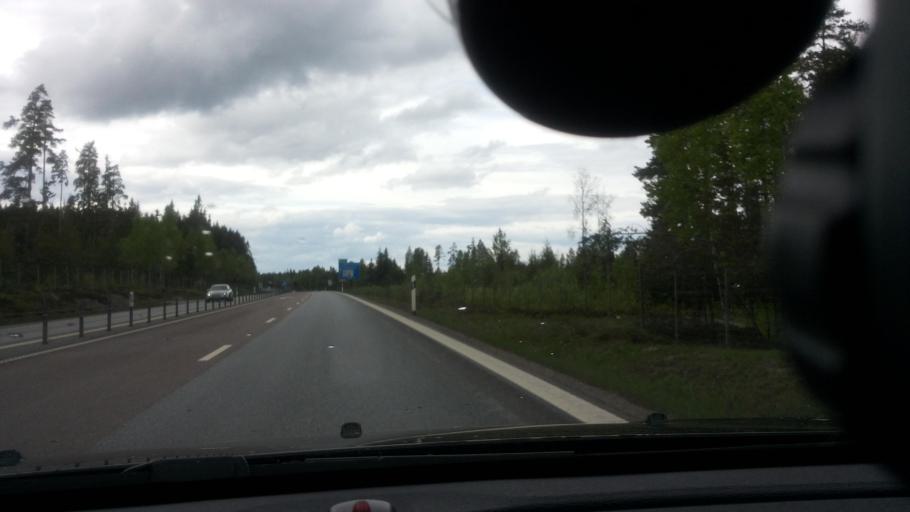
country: SE
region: Gaevleborg
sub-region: Gavle Kommun
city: Norrsundet
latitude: 60.8892
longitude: 17.0386
